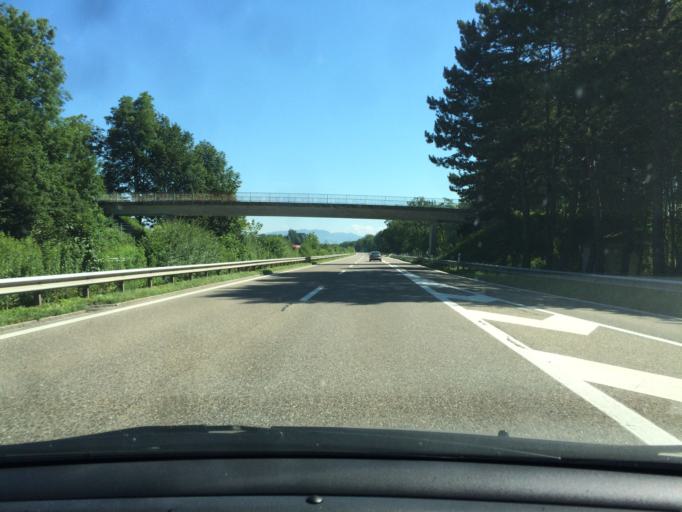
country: AT
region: Vorarlberg
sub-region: Politischer Bezirk Feldkirch
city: Mader
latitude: 47.3668
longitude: 9.6212
